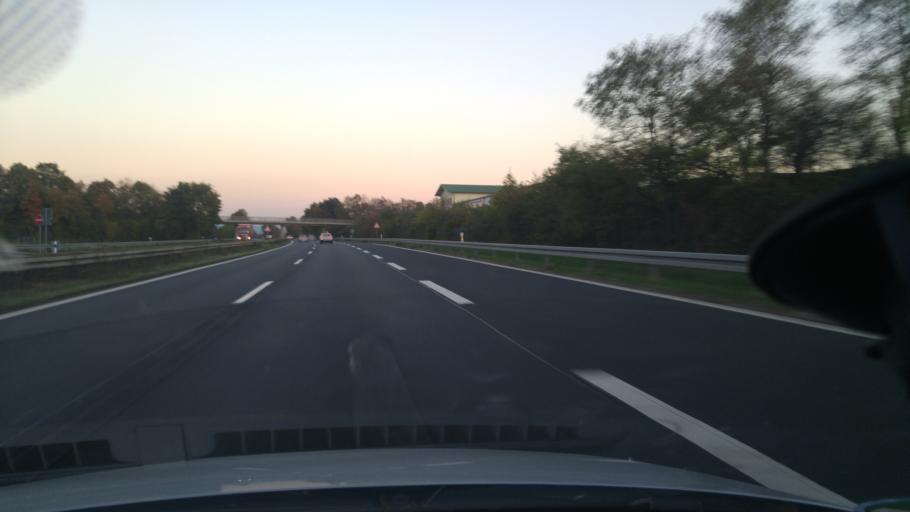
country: DE
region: Bavaria
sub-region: Regierungsbezirk Unterfranken
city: Grossostheim
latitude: 49.9437
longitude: 9.0647
